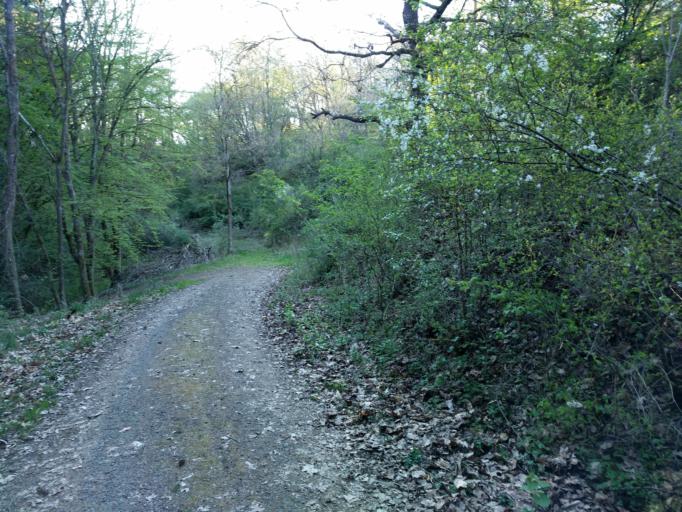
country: DE
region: Hesse
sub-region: Regierungsbezirk Giessen
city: Bad Endbach
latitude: 50.7612
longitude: 8.4847
